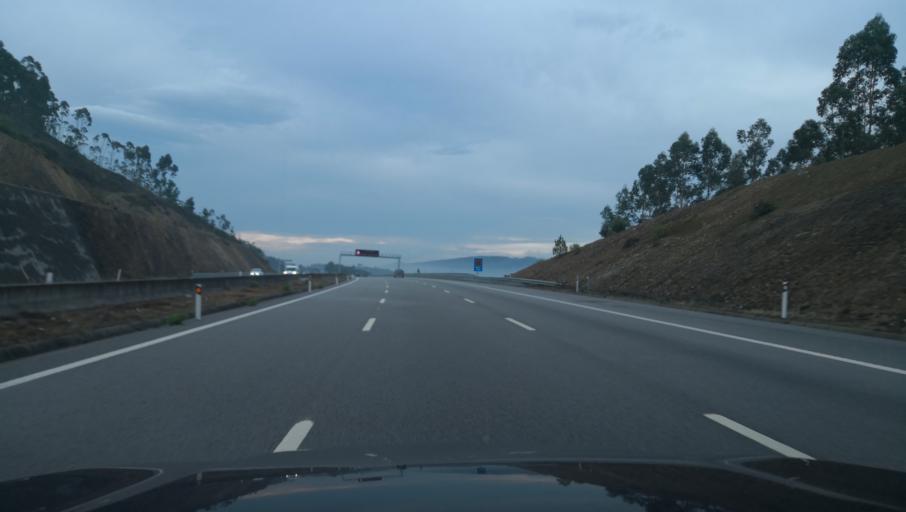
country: PT
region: Porto
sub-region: Paredes
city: Recarei
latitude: 41.1201
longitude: -8.4335
